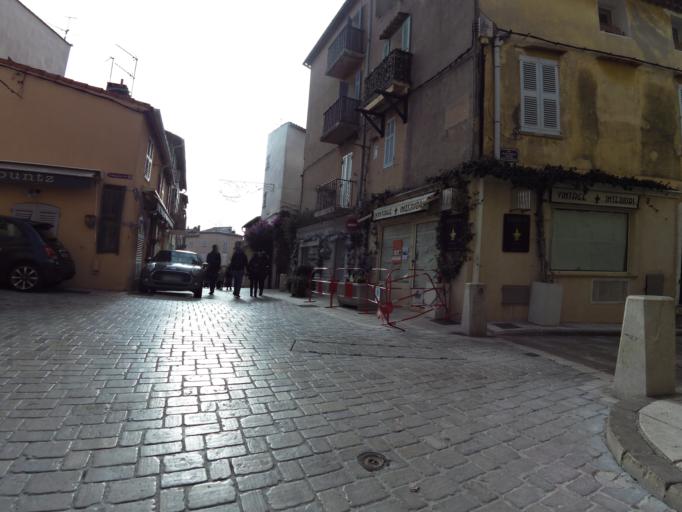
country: FR
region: Provence-Alpes-Cote d'Azur
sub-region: Departement du Var
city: Saint-Tropez
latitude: 43.2723
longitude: 6.6411
